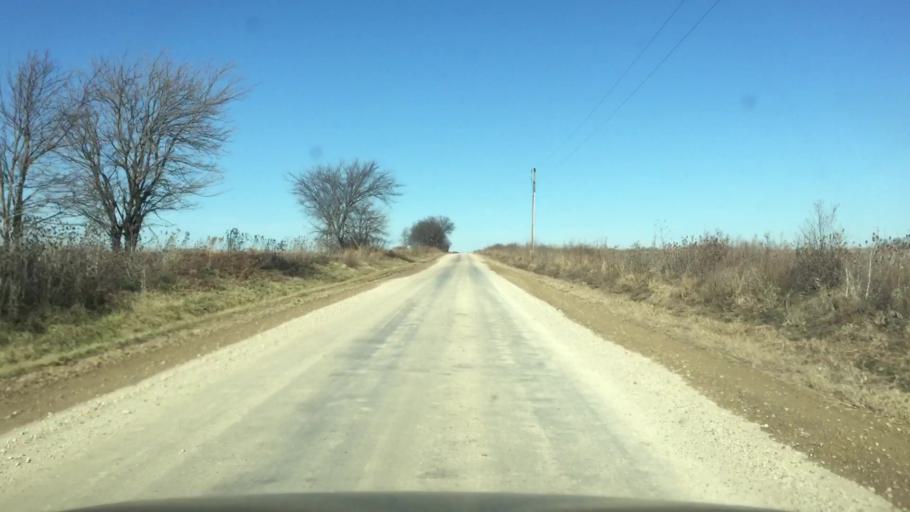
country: US
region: Kansas
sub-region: Allen County
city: Humboldt
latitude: 37.8545
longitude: -95.3910
